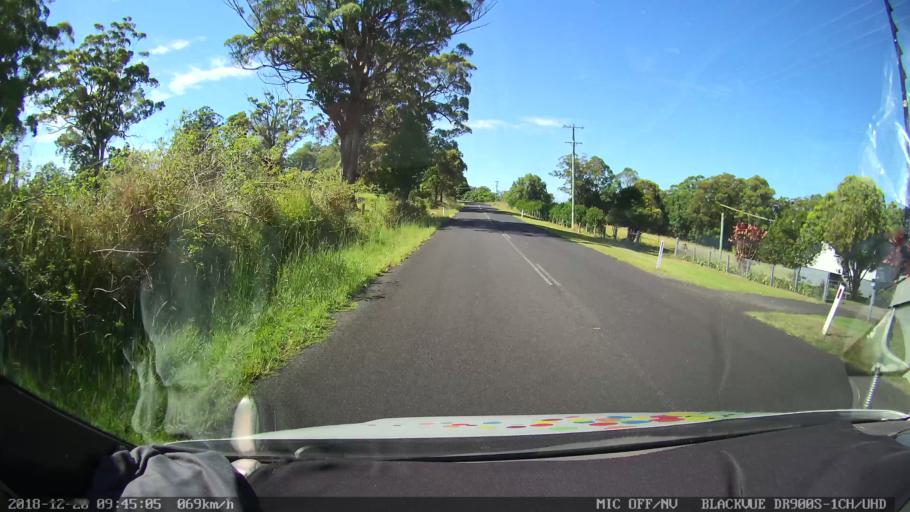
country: AU
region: New South Wales
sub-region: Lismore Municipality
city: Lismore
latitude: -28.7406
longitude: 153.2992
